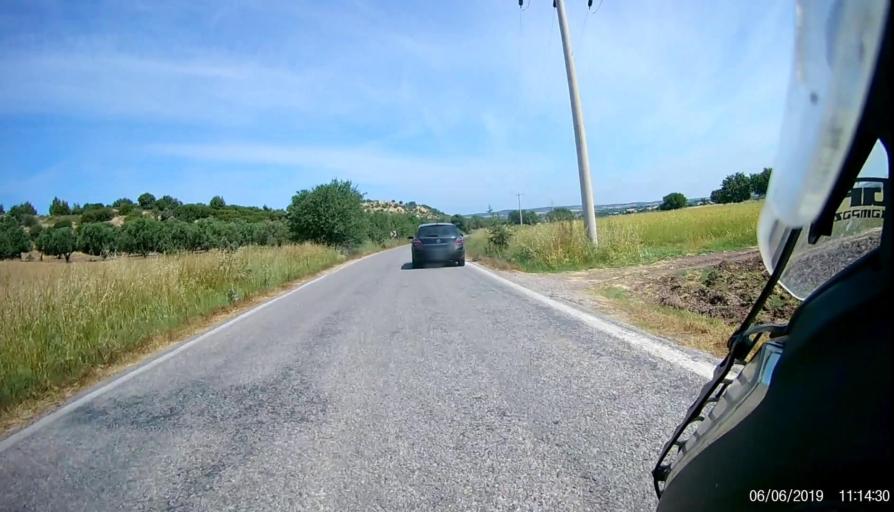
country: TR
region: Canakkale
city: Gulpinar
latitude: 39.6238
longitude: 26.1770
